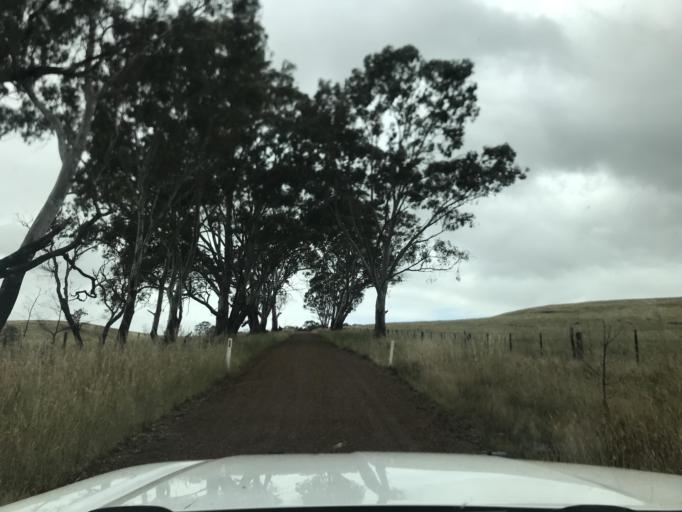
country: AU
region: South Australia
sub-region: Wattle Range
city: Penola
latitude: -37.2346
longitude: 141.4607
